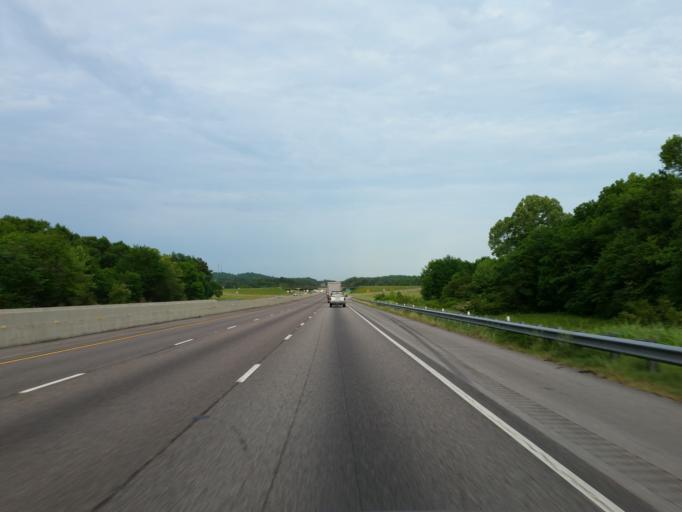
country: US
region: Alabama
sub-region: Calhoun County
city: Bynum
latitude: 33.5832
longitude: -86.0318
